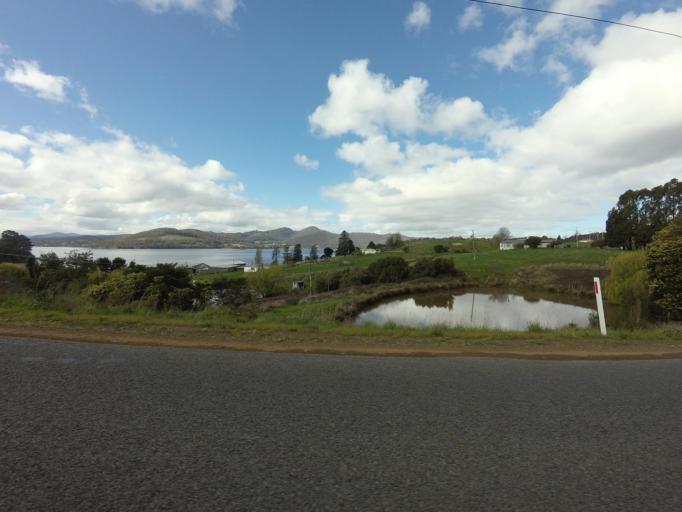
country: AU
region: Tasmania
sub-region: Huon Valley
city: Geeveston
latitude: -43.2059
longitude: 146.9693
